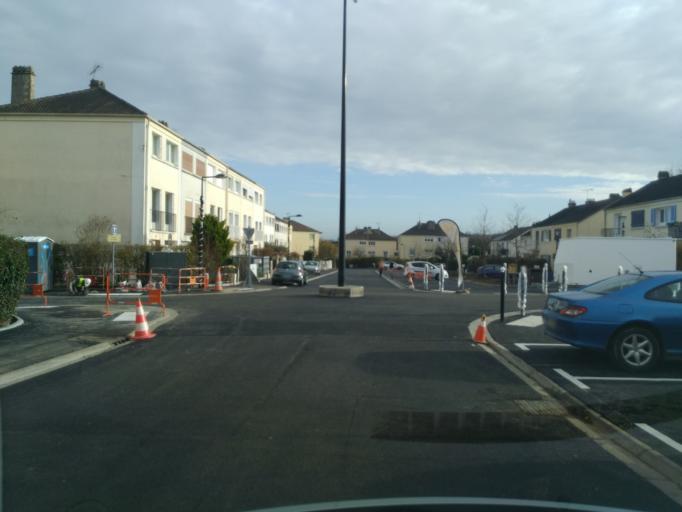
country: FR
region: Ile-de-France
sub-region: Departement des Yvelines
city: Villepreux
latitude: 48.8227
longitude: 1.9981
